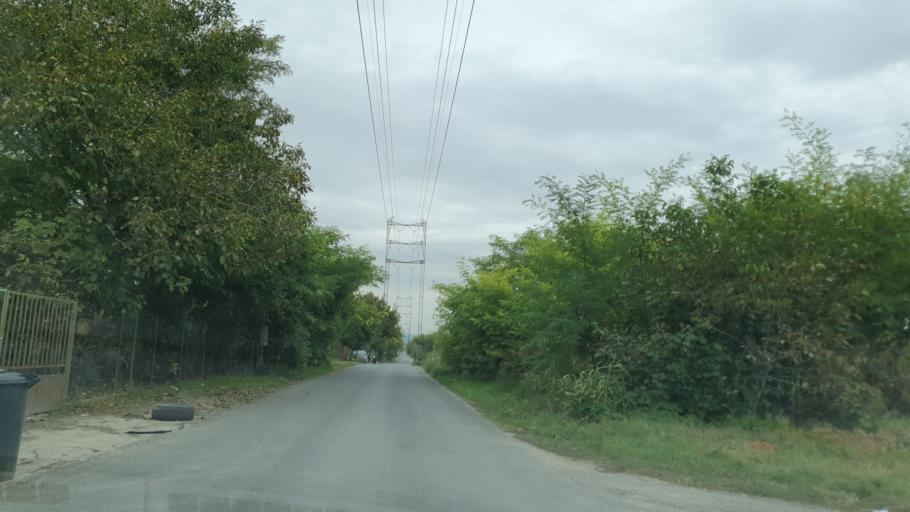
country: HU
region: Pest
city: Dunaharaszti
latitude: 47.3869
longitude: 19.0749
